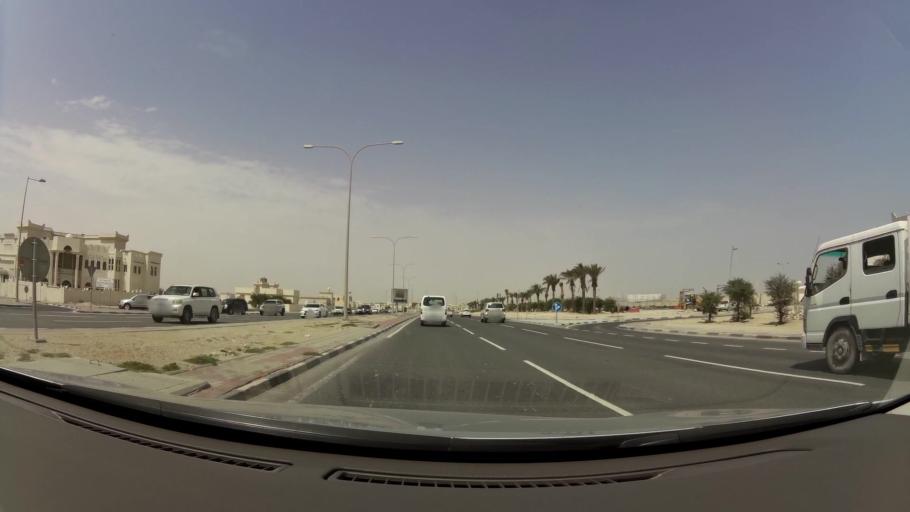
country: QA
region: Baladiyat ar Rayyan
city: Ar Rayyan
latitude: 25.3448
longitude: 51.4800
